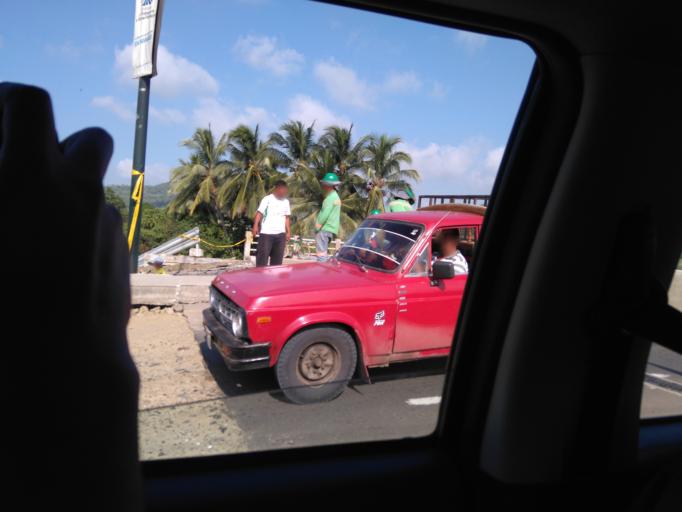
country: EC
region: Manabi
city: Portoviejo
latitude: -0.9901
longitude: -80.4695
